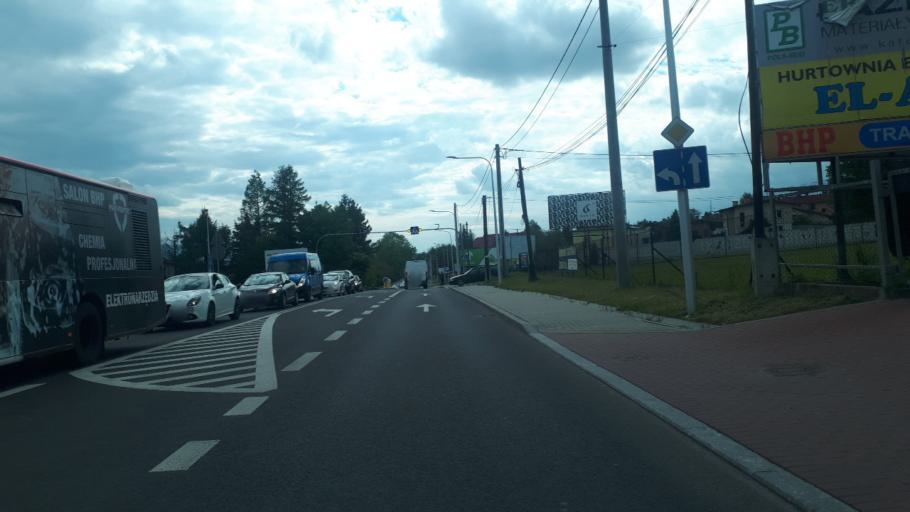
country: PL
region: Silesian Voivodeship
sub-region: Bielsko-Biala
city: Bielsko-Biala
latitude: 49.8229
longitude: 19.0826
